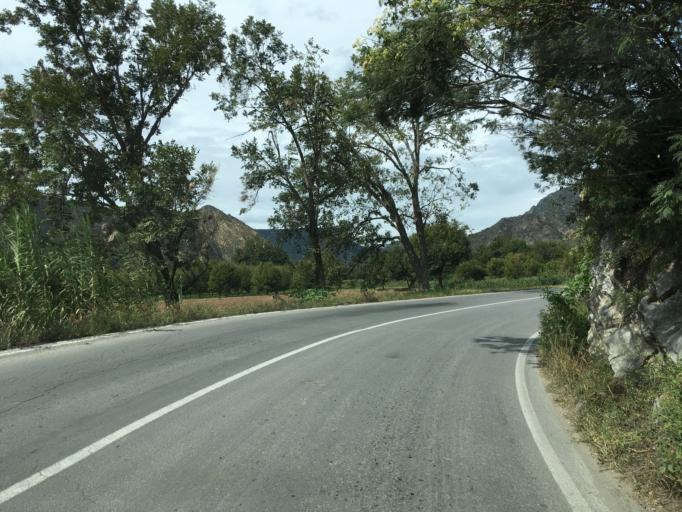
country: MX
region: Hidalgo
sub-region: San Agustin Metzquititlan
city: Mezquititlan
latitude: 20.5382
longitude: -98.7255
